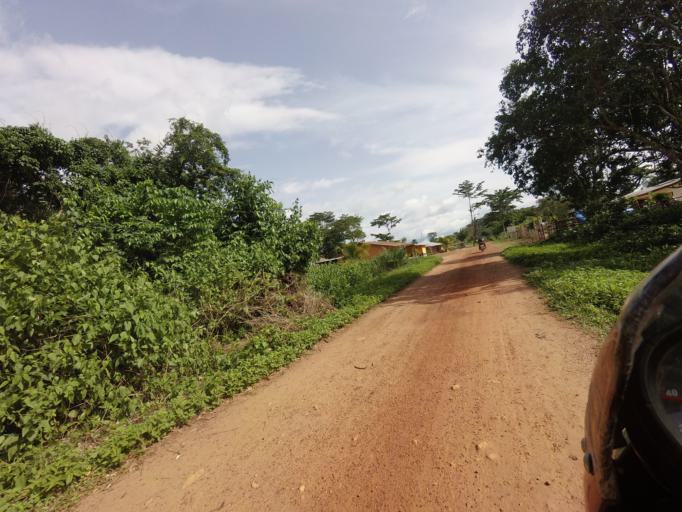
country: SL
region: Eastern Province
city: Jojoima
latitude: 7.8264
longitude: -10.8131
